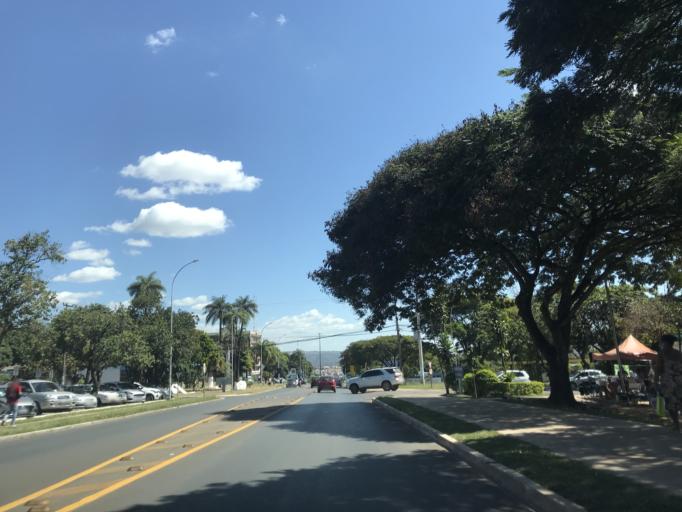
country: BR
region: Federal District
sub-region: Brasilia
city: Brasilia
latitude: -15.6497
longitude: -47.7925
